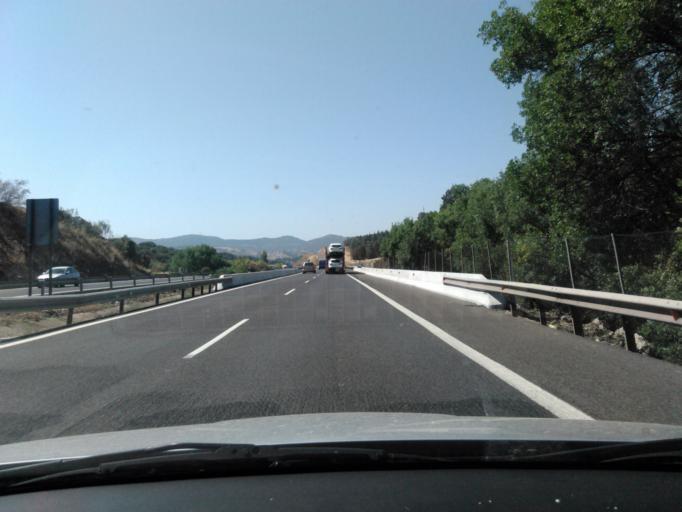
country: ES
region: Castille-La Mancha
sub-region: Provincia de Ciudad Real
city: Viso del Marques
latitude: 38.4493
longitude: -3.4970
